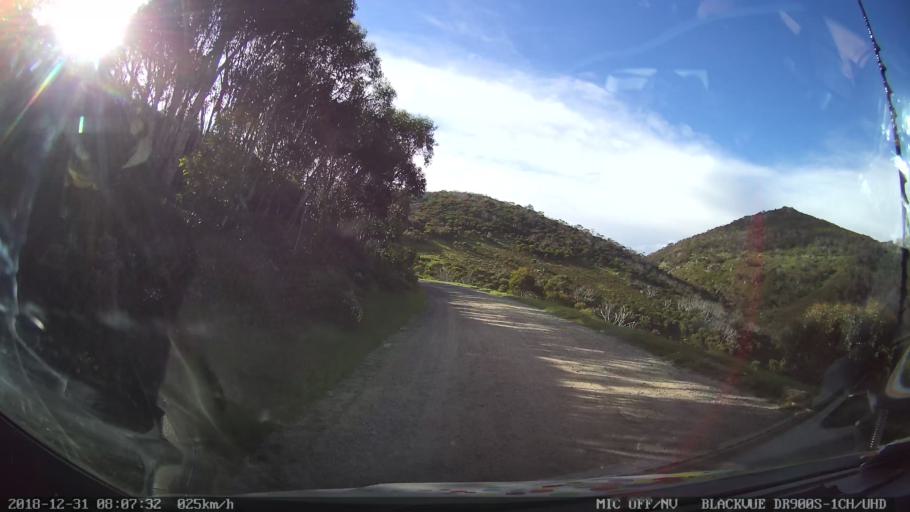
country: AU
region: New South Wales
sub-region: Snowy River
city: Jindabyne
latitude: -36.3792
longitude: 148.4093
